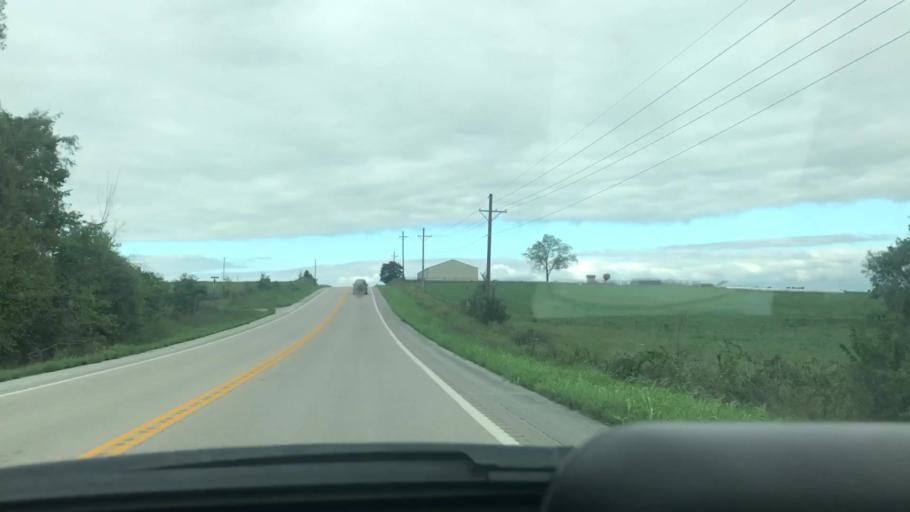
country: US
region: Missouri
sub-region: Hickory County
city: Hermitage
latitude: 37.8819
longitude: -93.1802
